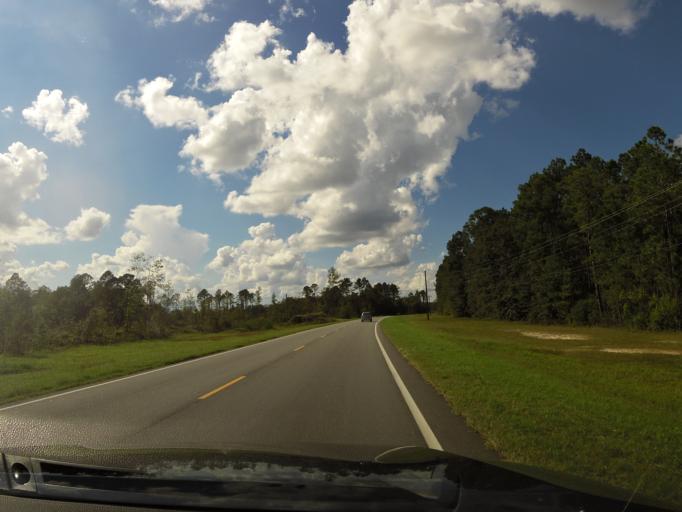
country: US
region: Georgia
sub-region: Echols County
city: Statenville
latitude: 30.7074
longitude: -83.0531
